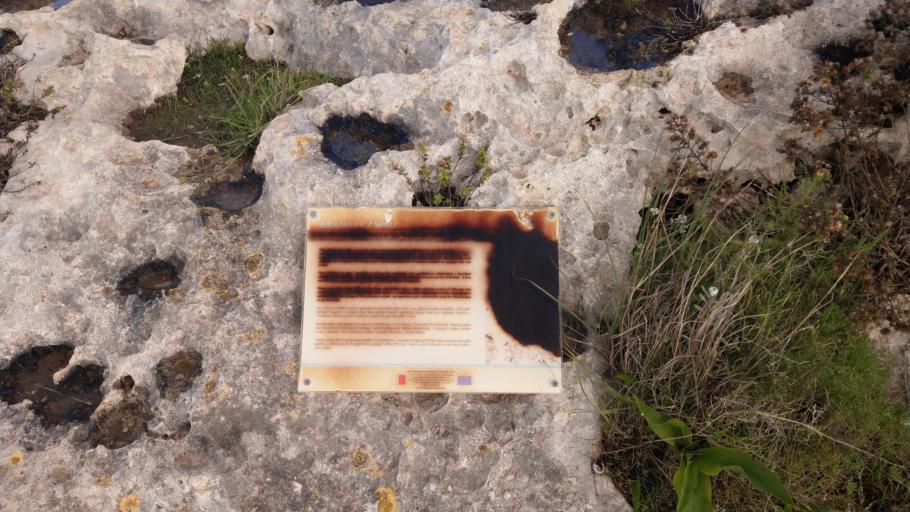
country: MT
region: Il-Mellieha
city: Mellieha
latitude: 35.9497
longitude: 14.3815
